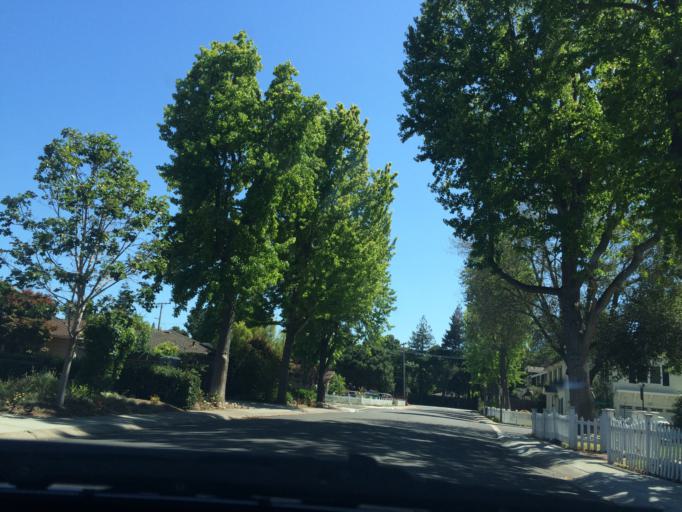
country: US
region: California
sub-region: San Mateo County
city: North Fair Oaks
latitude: 37.4768
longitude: -122.1747
